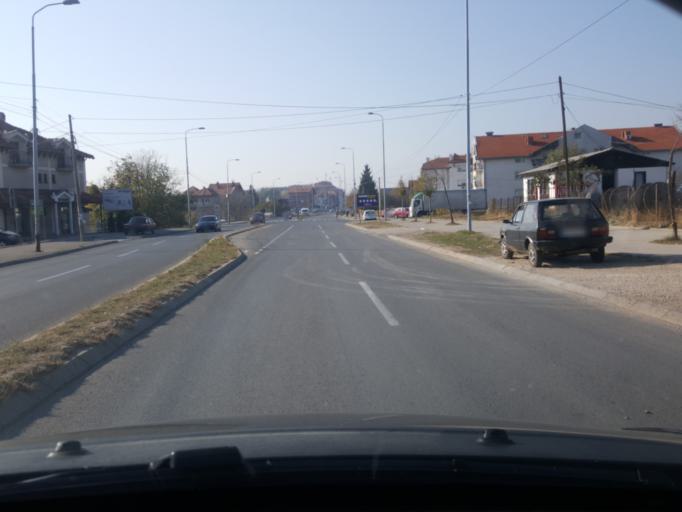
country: RS
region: Central Serbia
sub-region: Nisavski Okrug
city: Nis
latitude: 43.3303
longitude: 21.9454
